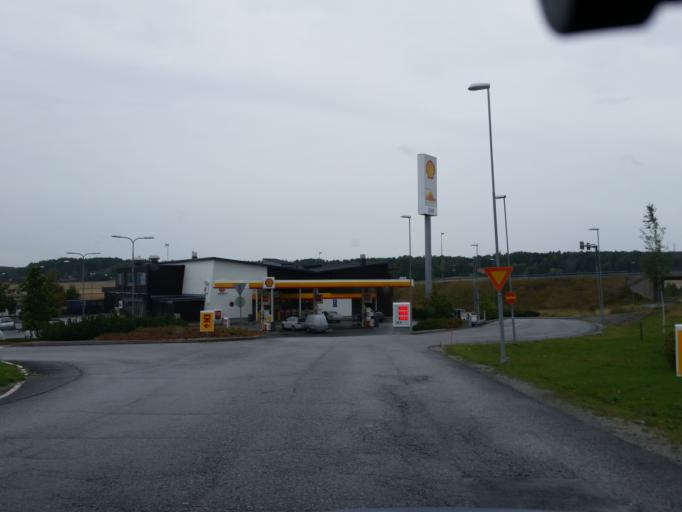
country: FI
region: Varsinais-Suomi
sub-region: Salo
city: Halikko
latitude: 60.4245
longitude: 23.0463
